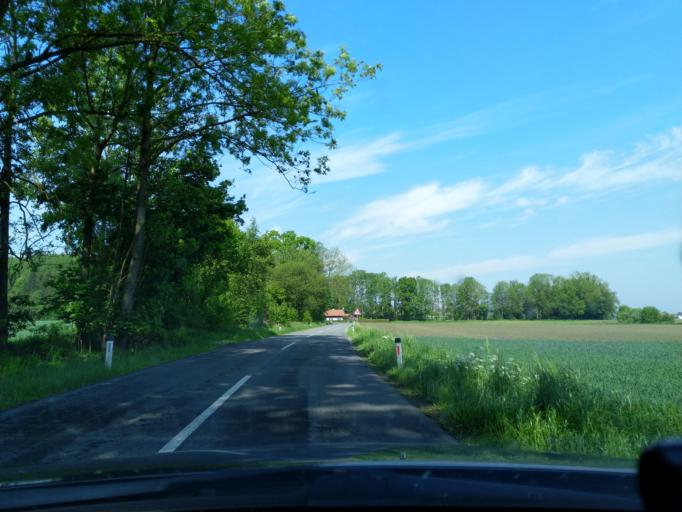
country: AT
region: Upper Austria
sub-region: Politischer Bezirk Scharding
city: Sankt Marienkirchen bei Schaerding
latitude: 48.2956
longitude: 13.4274
